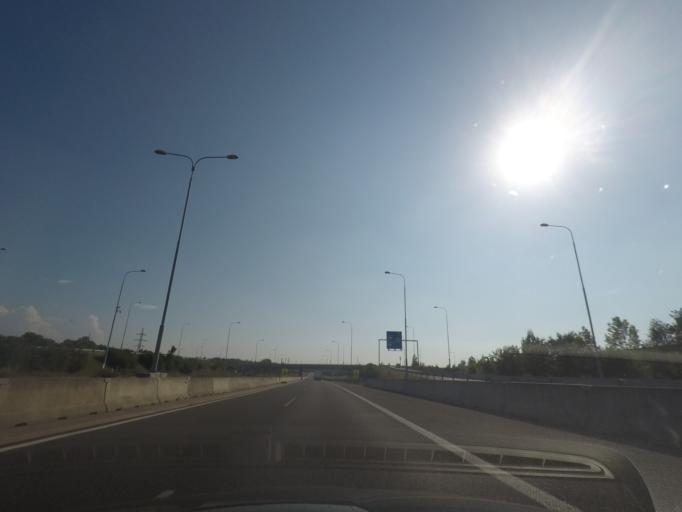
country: CZ
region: Moravskoslezsky
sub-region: Okres Ostrava-Mesto
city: Ostrava
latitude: 49.8592
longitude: 18.2581
